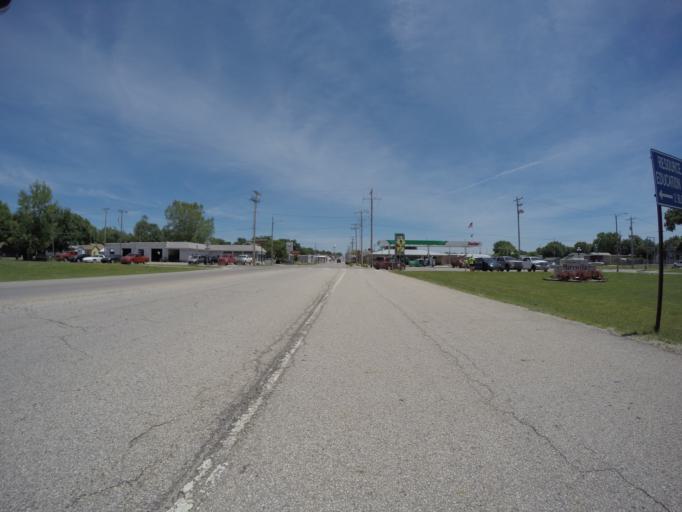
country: US
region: Kansas
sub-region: Marshall County
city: Marysville
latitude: 39.8421
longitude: -96.6535
